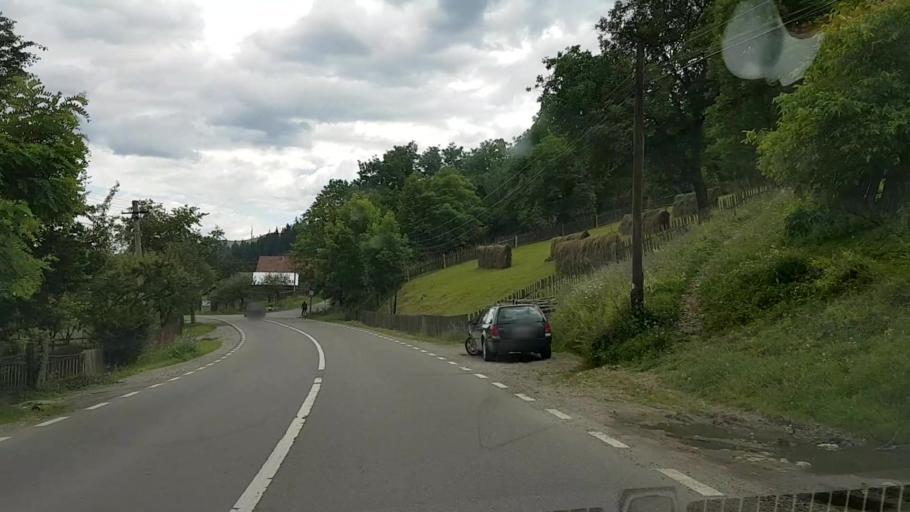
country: RO
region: Neamt
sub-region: Comuna Borca
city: Borca
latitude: 47.1854
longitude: 25.7745
